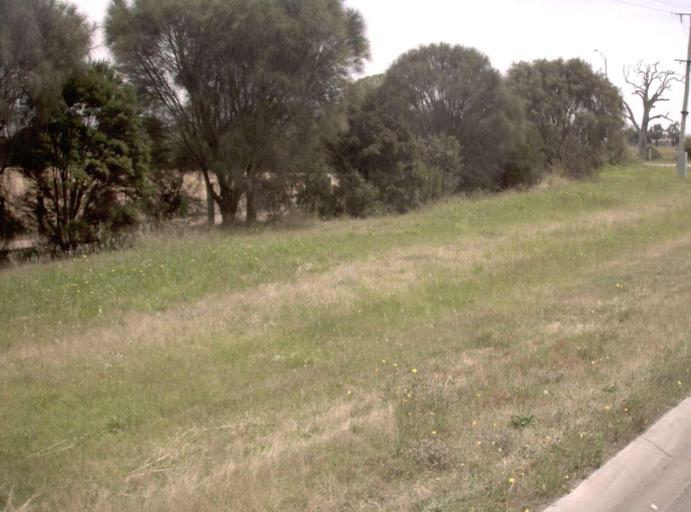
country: AU
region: Victoria
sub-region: Casey
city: Lynbrook
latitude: -38.0636
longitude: 145.2420
